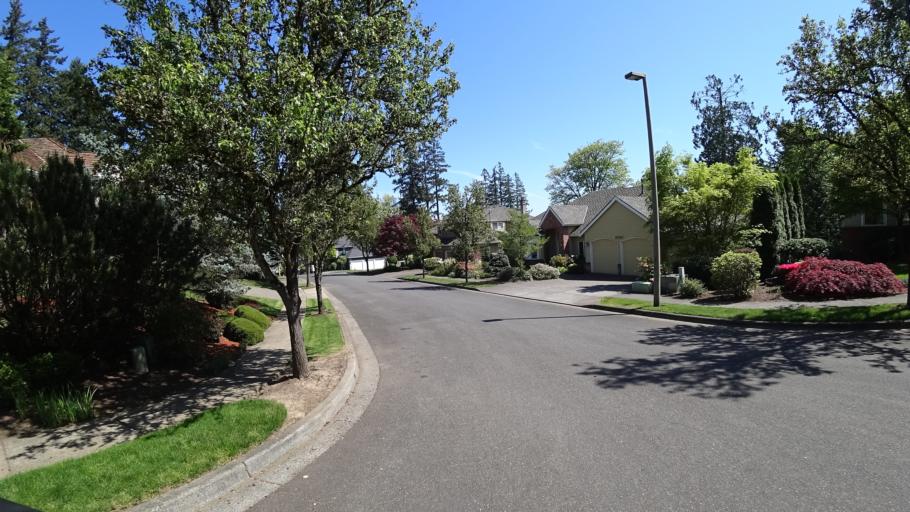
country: US
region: Oregon
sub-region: Washington County
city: Aloha
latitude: 45.4472
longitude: -122.8458
